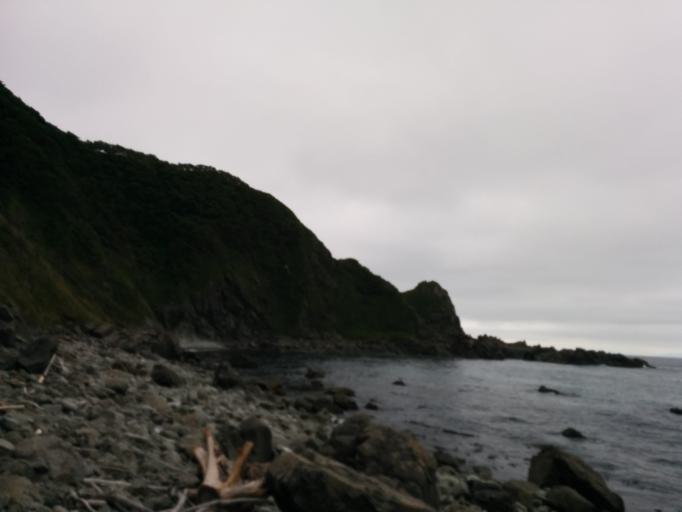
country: JP
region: Hokkaido
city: Iwanai
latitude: 42.3087
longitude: 139.7685
